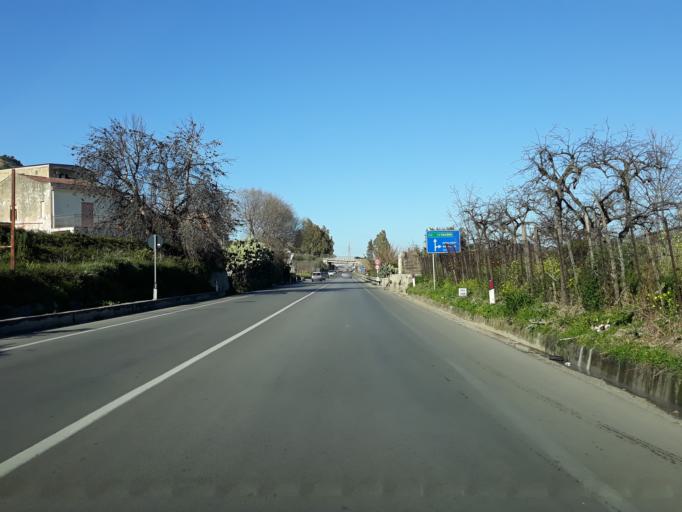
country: IT
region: Sicily
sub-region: Palermo
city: Misilmeri
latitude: 38.0332
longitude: 13.4580
